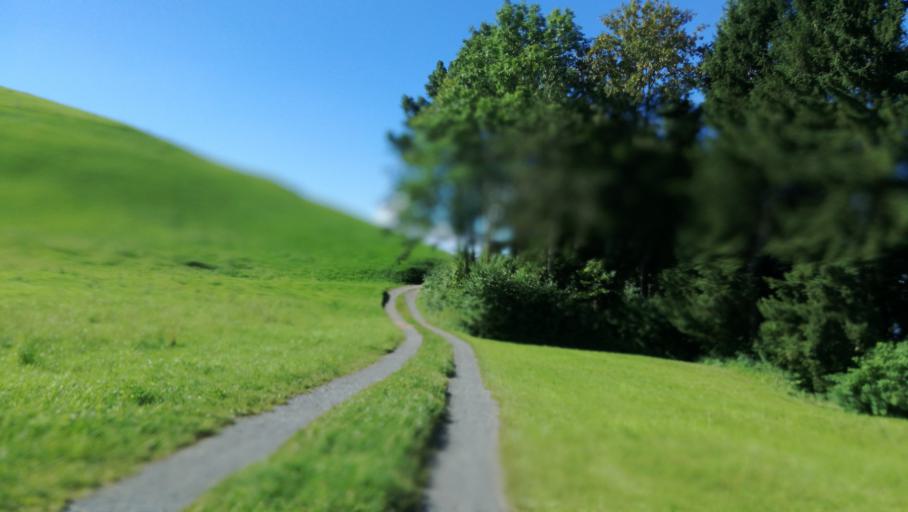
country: CH
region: Zug
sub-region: Zug
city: Unterageri
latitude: 47.1566
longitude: 8.5556
